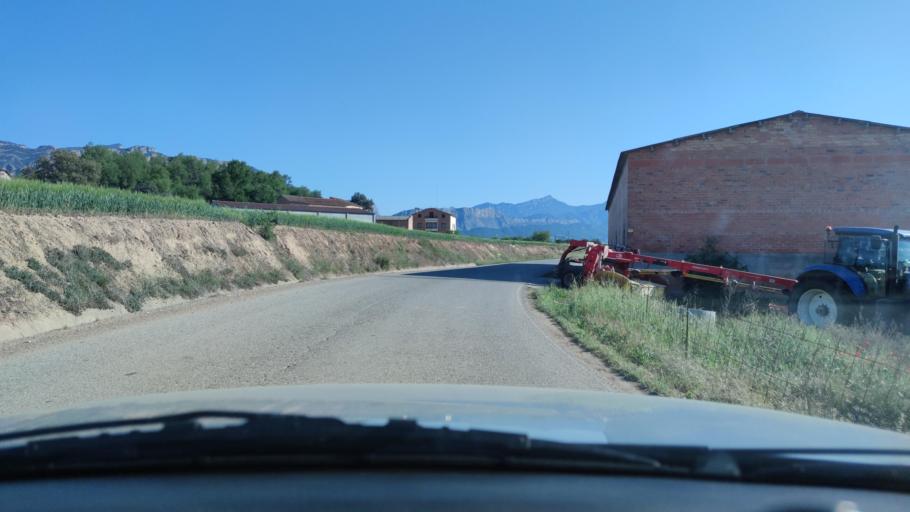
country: ES
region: Catalonia
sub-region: Provincia de Lleida
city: Oliana
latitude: 42.0448
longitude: 1.2917
